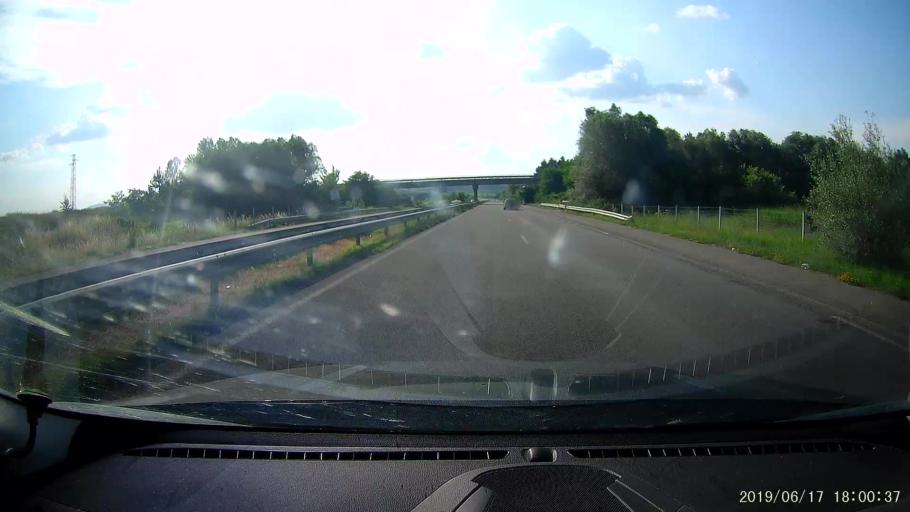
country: BG
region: Khaskovo
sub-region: Obshtina Svilengrad
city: Svilengrad
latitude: 41.7386
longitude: 26.2753
